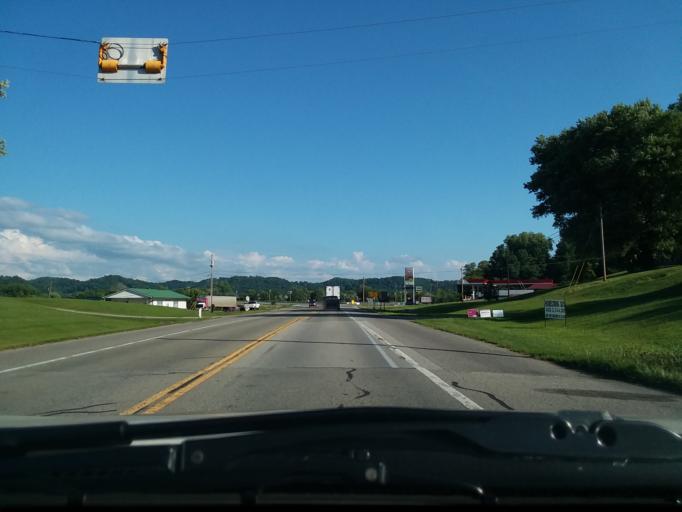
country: US
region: Tennessee
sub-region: Clay County
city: Celina
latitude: 36.5586
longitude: -85.5196
